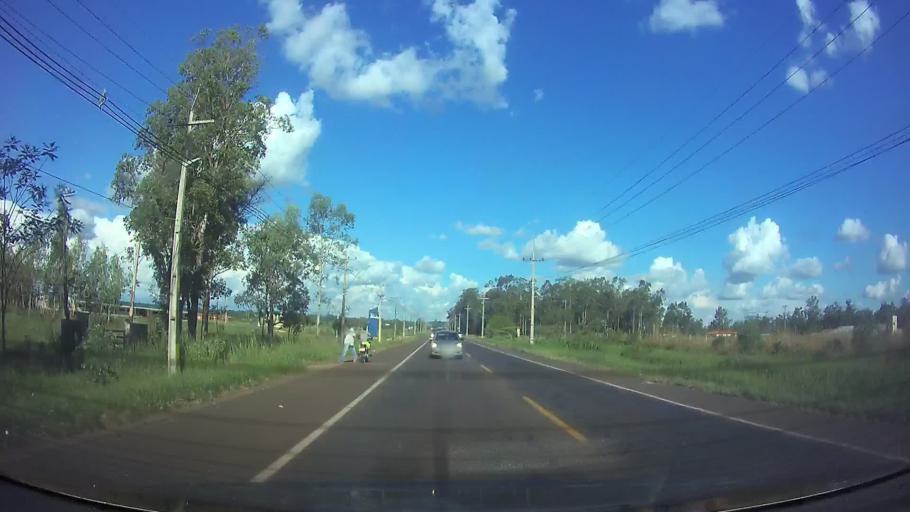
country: PY
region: Cordillera
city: Eusebio Ayala
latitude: -25.3807
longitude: -56.9840
